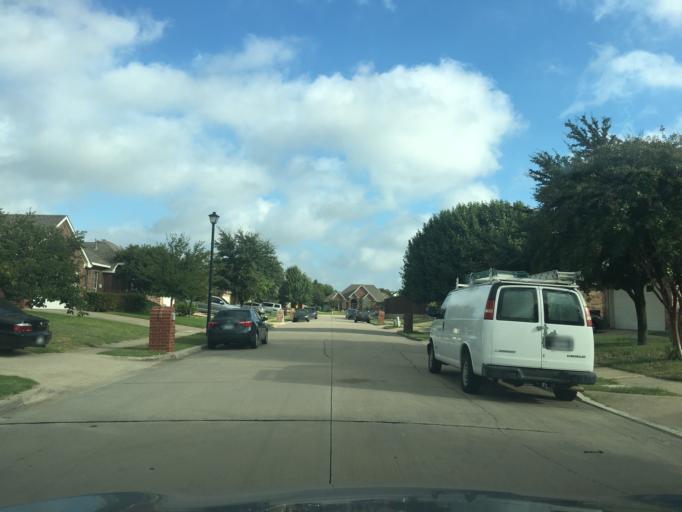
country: US
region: Texas
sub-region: Dallas County
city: Sachse
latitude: 32.9652
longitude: -96.5980
